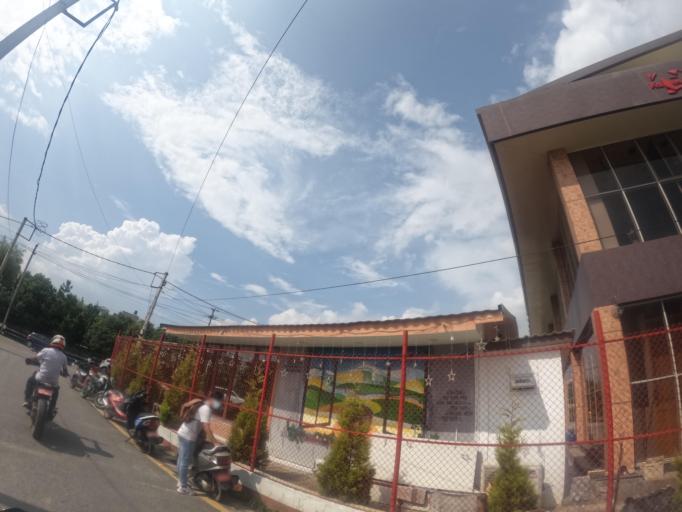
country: NP
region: Central Region
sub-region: Bagmati Zone
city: Kathmandu
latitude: 27.6875
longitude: 85.3668
